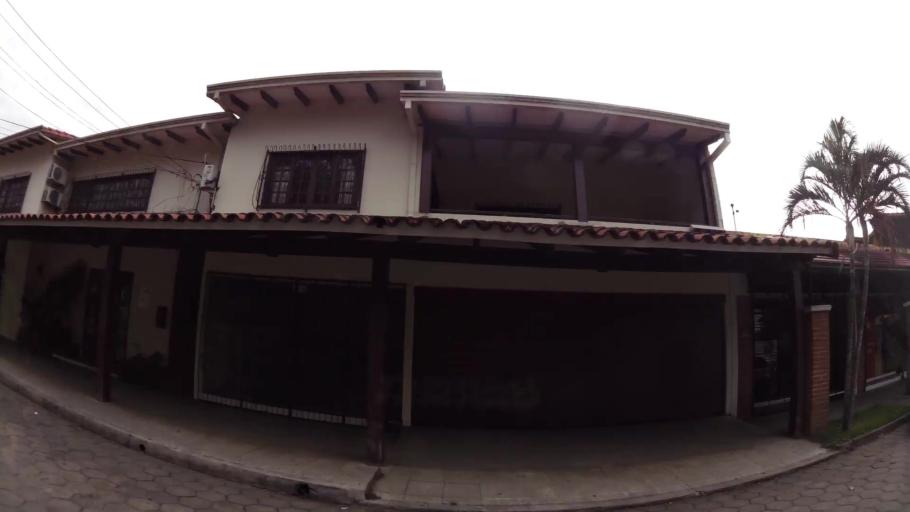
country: BO
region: Santa Cruz
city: Santa Cruz de la Sierra
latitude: -17.7883
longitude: -63.1751
